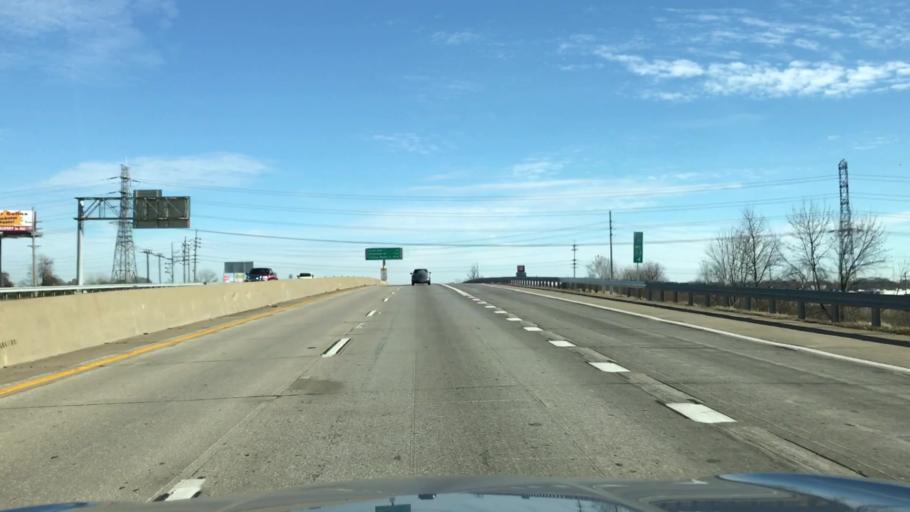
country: US
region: Missouri
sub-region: Saint Louis County
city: Glasgow Village
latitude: 38.7682
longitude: -90.2113
